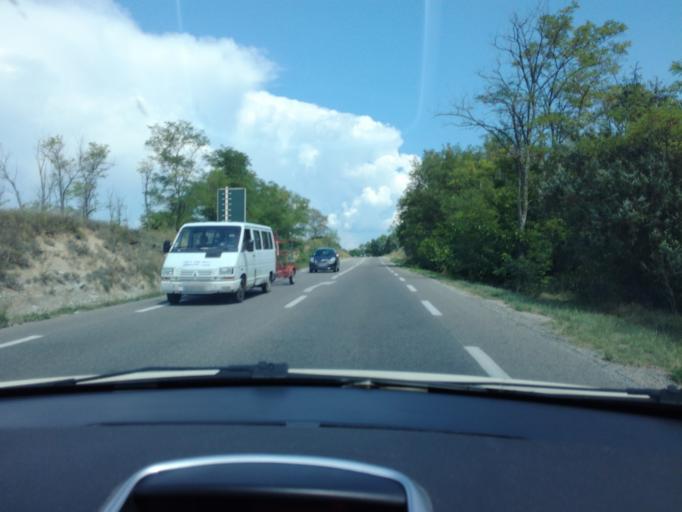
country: FR
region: Rhone-Alpes
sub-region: Departement de l'Ardeche
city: Ruoms
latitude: 44.4988
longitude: 4.3854
